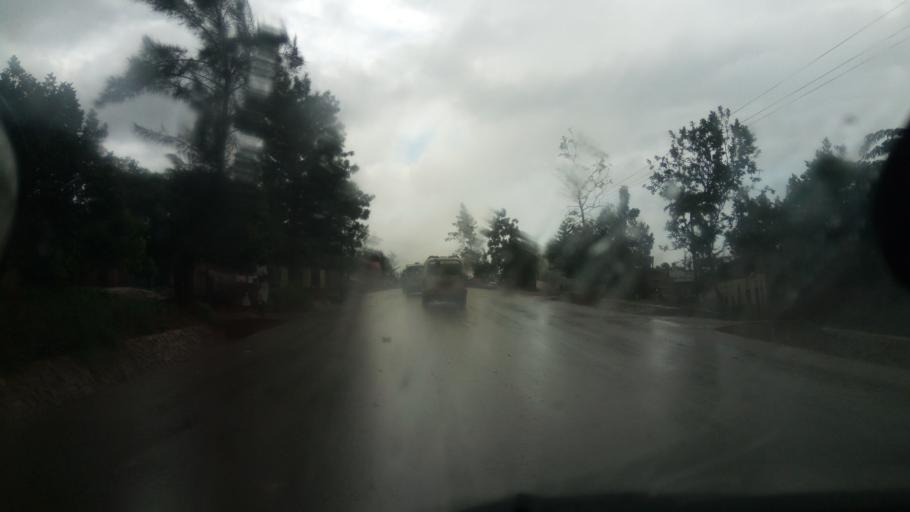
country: UG
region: Central Region
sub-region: Wakiso District
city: Wakiso
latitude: 0.4052
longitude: 32.4721
